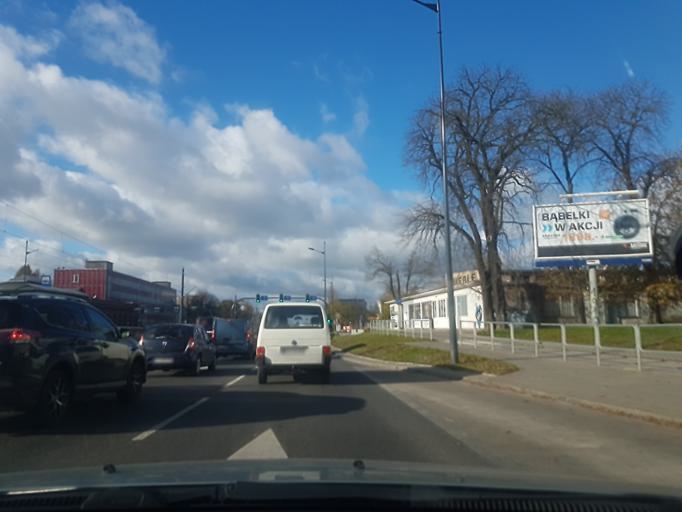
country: PL
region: Lodz Voivodeship
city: Lodz
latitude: 51.7631
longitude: 19.5020
